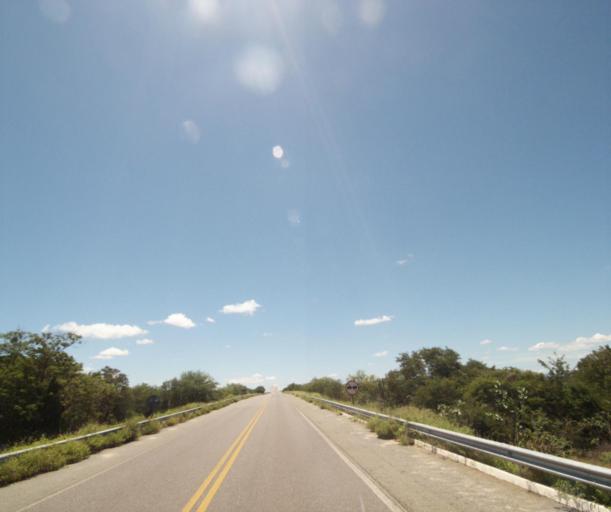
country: BR
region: Bahia
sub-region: Carinhanha
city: Carinhanha
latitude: -14.3211
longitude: -43.7770
